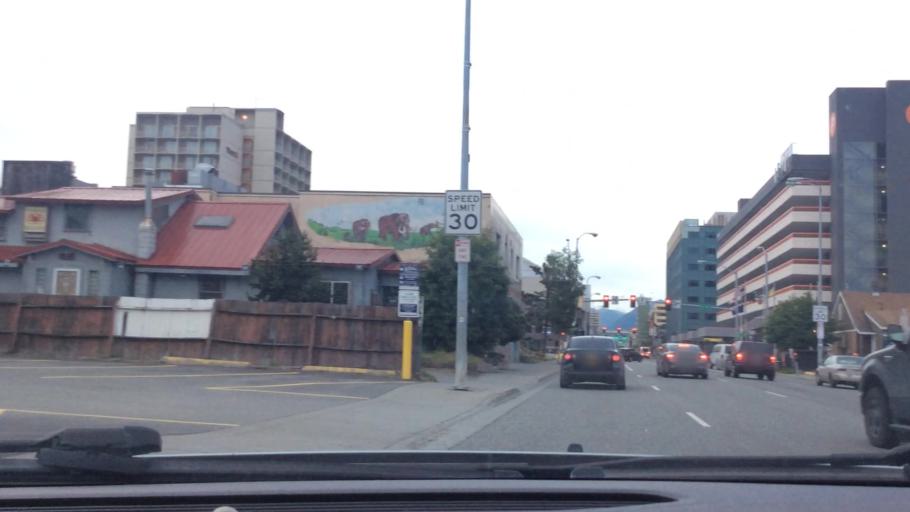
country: US
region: Alaska
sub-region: Anchorage Municipality
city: Anchorage
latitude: 61.2167
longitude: -149.8992
